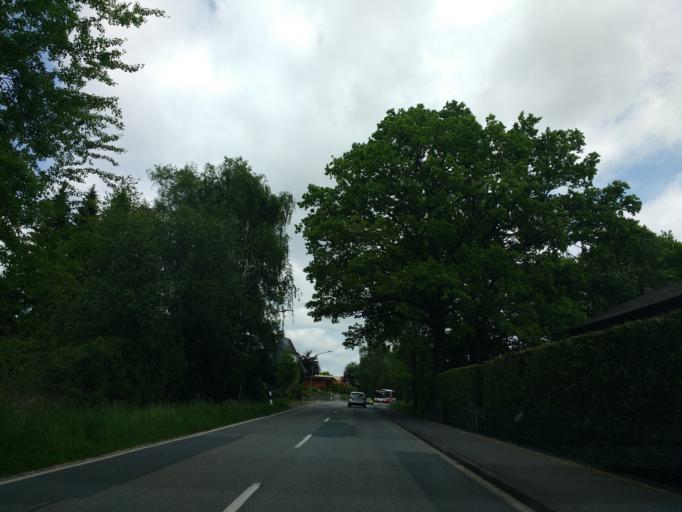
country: DE
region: Schleswig-Holstein
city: Stapelfeld
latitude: 53.5681
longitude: 10.2240
